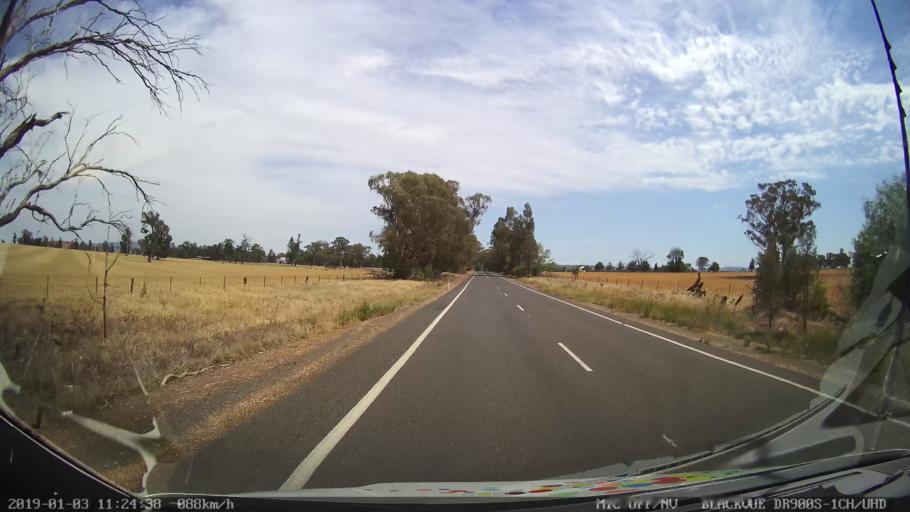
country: AU
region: New South Wales
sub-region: Weddin
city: Grenfell
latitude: -34.0489
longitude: 148.2337
